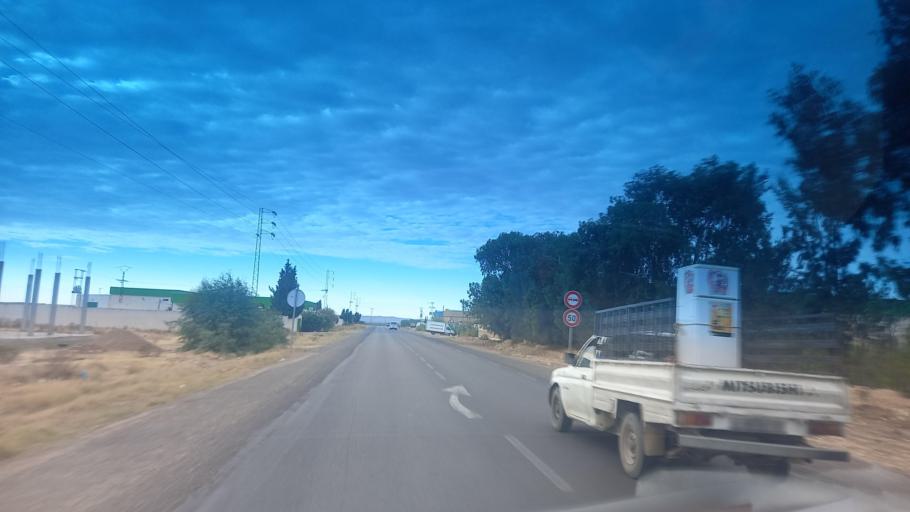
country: TN
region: Al Qasrayn
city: Sbiba
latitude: 35.2856
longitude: 9.0930
